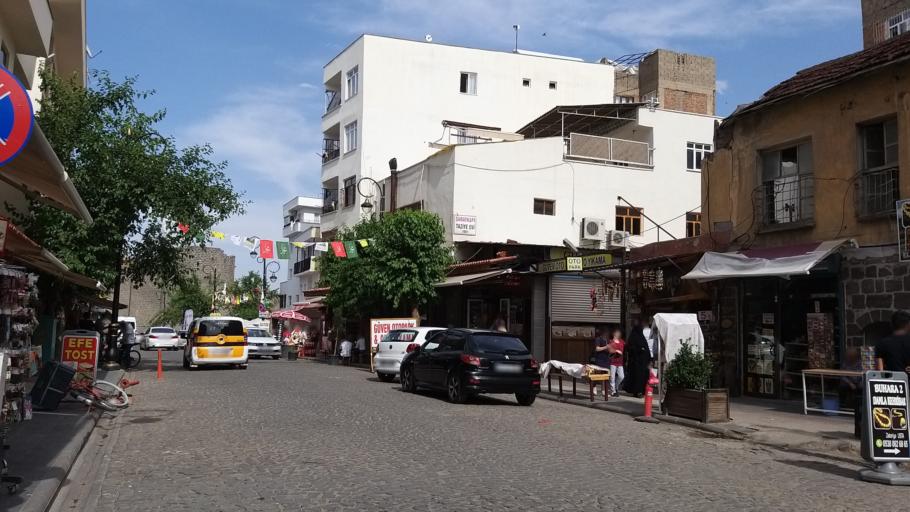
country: TR
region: Diyarbakir
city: Sur
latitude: 37.9148
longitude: 40.2387
